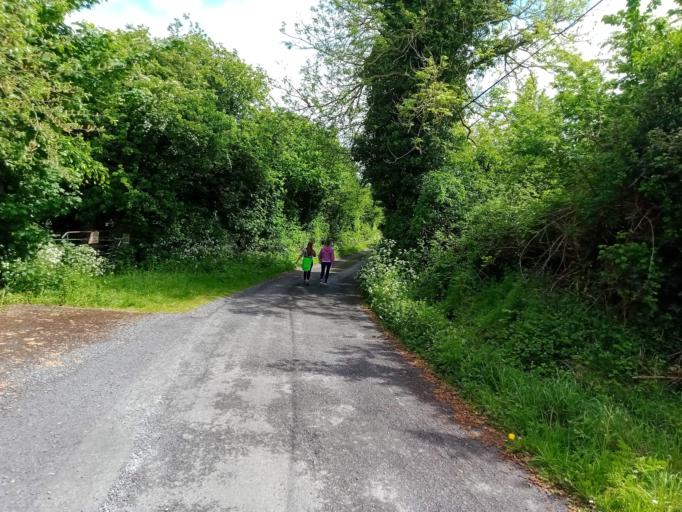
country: IE
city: Ballylinan
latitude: 52.9651
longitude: -7.0736
